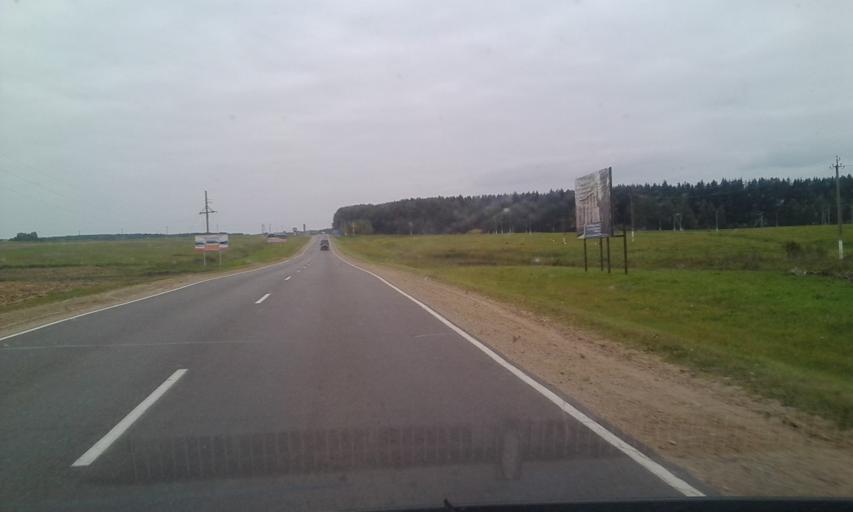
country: BY
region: Vitebsk
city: Pastavy
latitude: 55.1068
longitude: 26.8736
